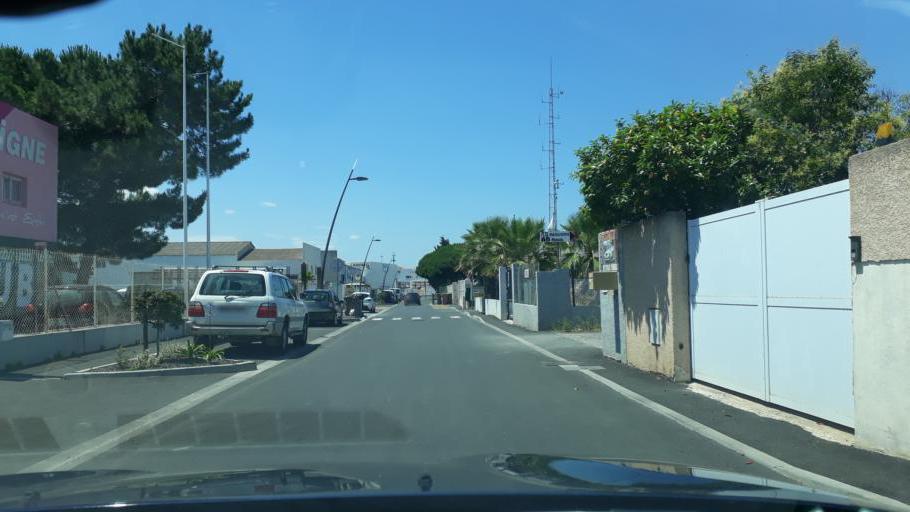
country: FR
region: Languedoc-Roussillon
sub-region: Departement de l'Herault
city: Agde
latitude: 43.3095
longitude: 3.4943
